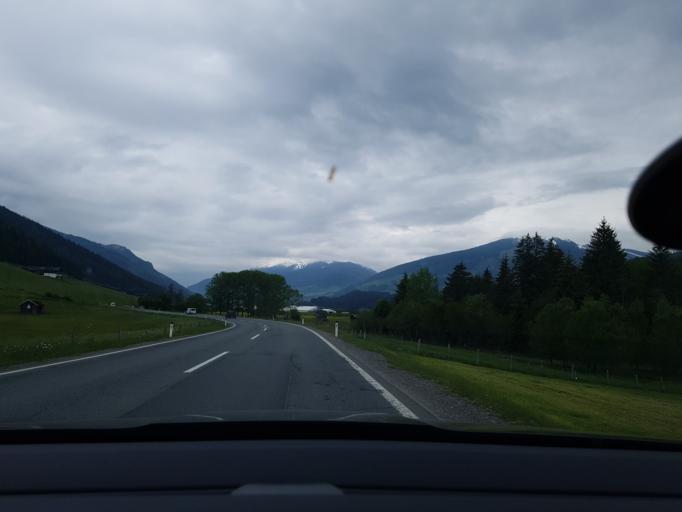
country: AT
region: Salzburg
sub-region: Politischer Bezirk Zell am See
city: Mittersill
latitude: 47.2779
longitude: 12.4652
